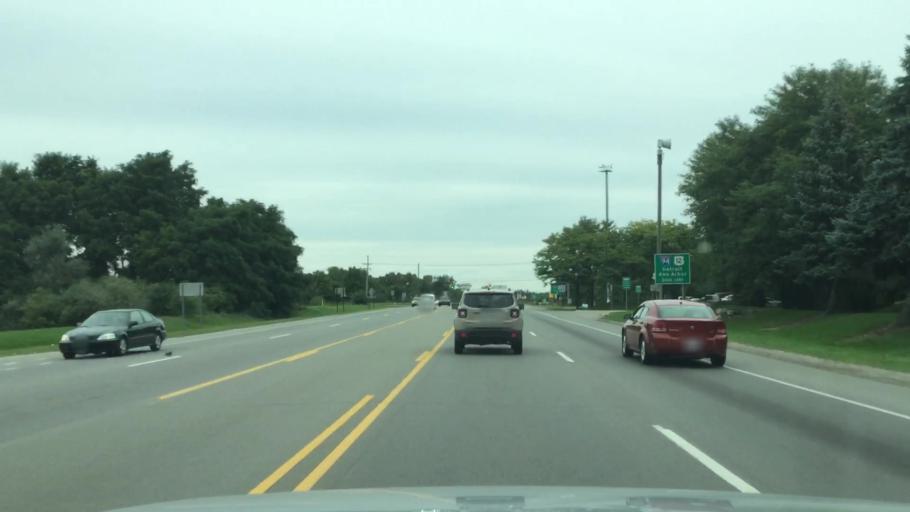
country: US
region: Michigan
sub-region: Washtenaw County
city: Ypsilanti
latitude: 42.2247
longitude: -83.6177
